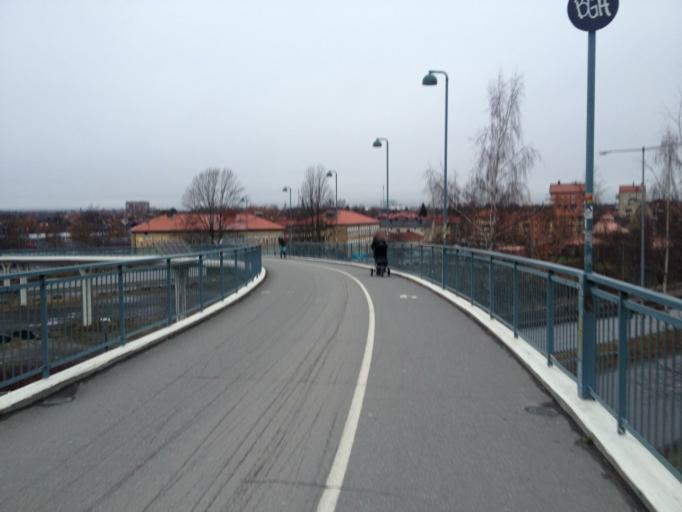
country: SE
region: Vaesterbotten
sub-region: Umea Kommun
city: Umea
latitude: 63.8197
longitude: 20.2945
